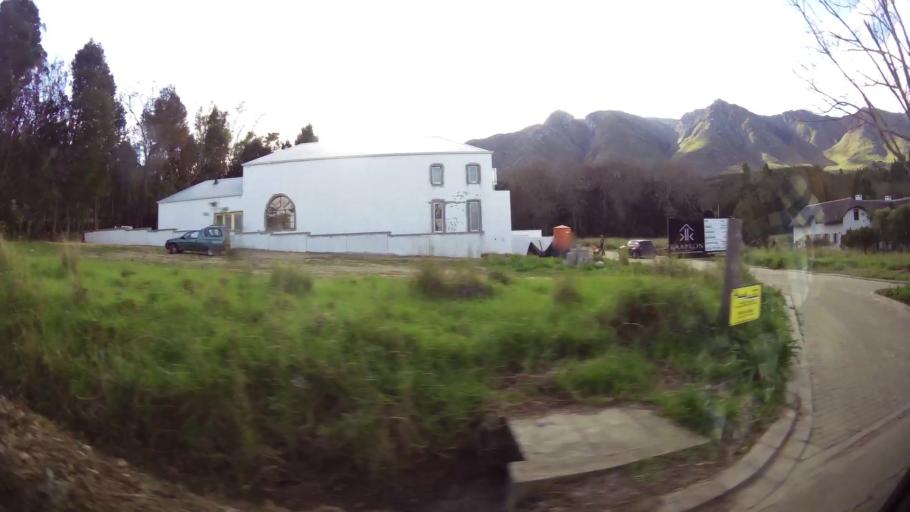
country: ZA
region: Western Cape
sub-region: Overberg District Municipality
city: Swellendam
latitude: -34.0128
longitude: 20.4496
